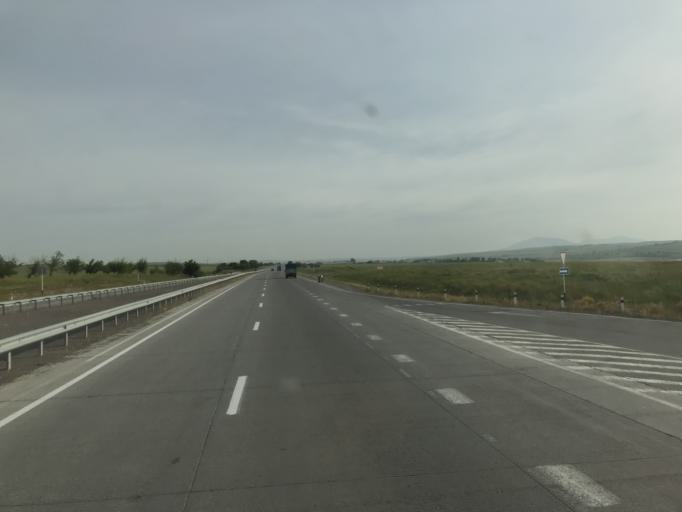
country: KZ
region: Ongtustik Qazaqstan
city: Qazyqurt
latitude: 41.8101
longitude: 69.3969
